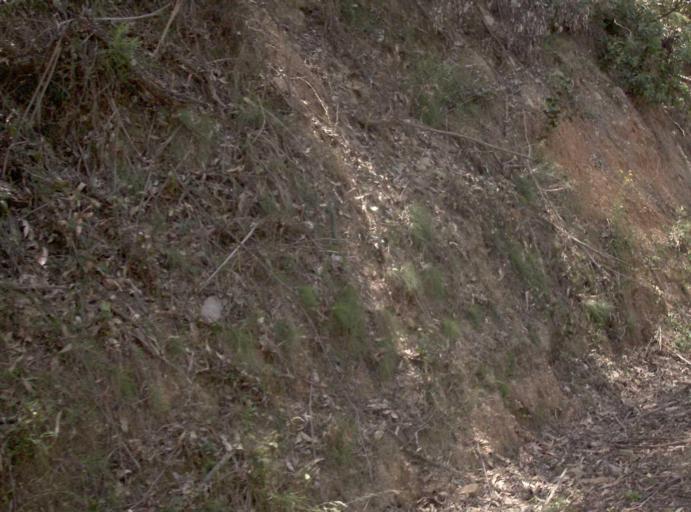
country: AU
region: New South Wales
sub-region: Bombala
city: Bombala
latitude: -37.4535
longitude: 148.9310
